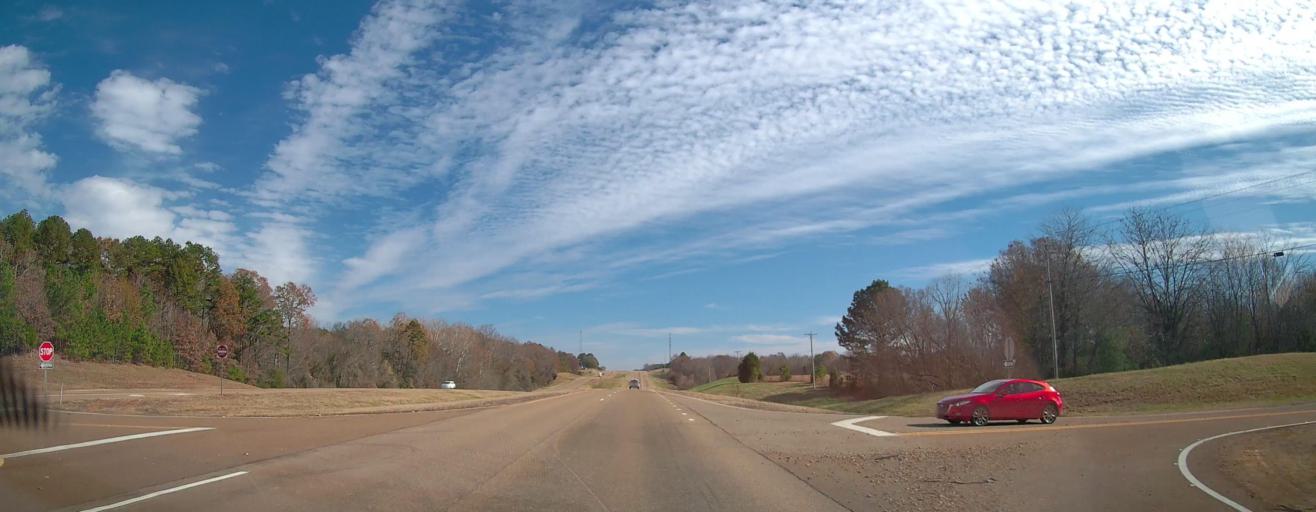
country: US
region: Mississippi
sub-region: Benton County
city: Ashland
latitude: 34.9457
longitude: -89.1597
